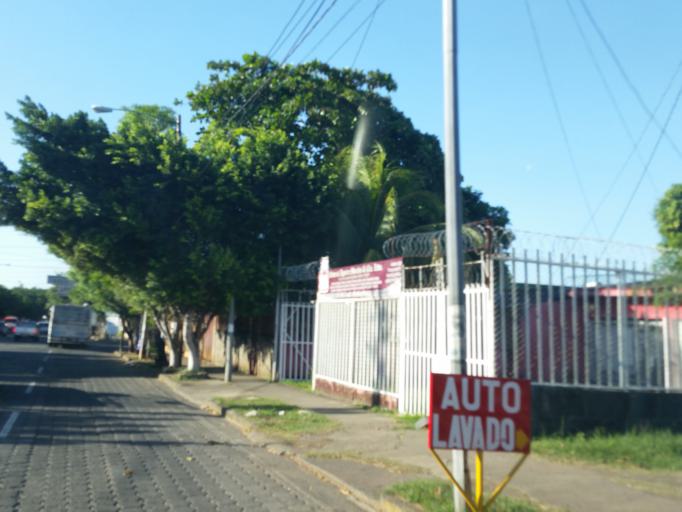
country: NI
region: Managua
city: Managua
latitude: 12.1424
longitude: -86.2959
